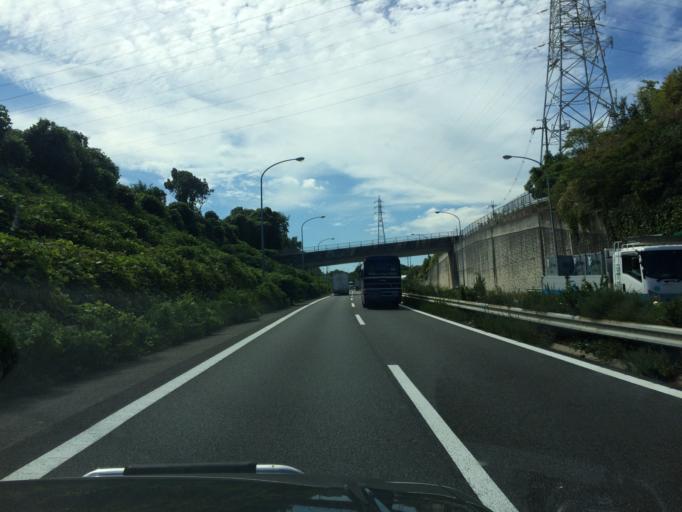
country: JP
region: Osaka
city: Izumi
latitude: 34.4477
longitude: 135.4451
